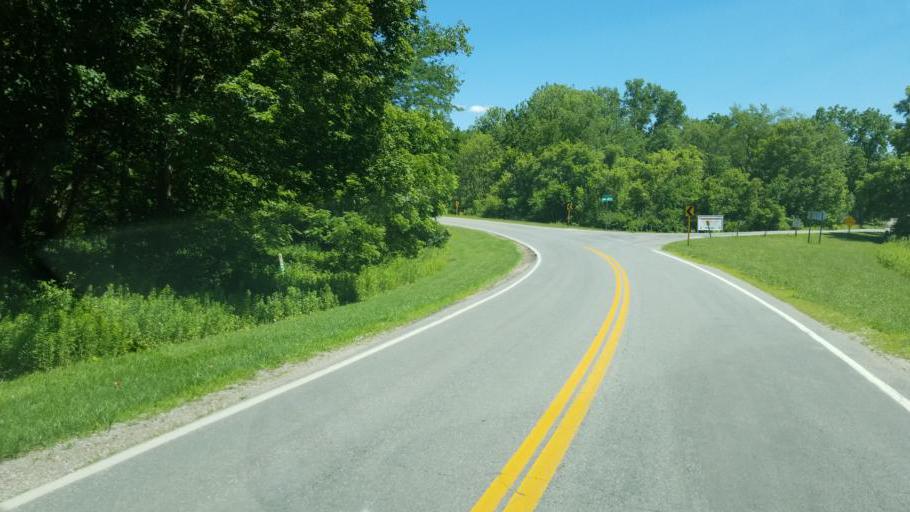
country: US
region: Ohio
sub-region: Delaware County
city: Sunbury
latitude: 40.2370
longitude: -82.8982
